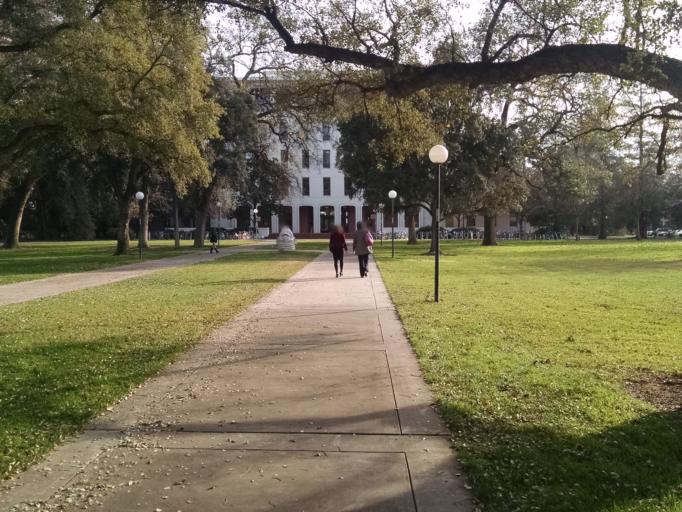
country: US
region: California
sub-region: Yolo County
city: Davis
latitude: 38.5381
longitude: -121.7496
